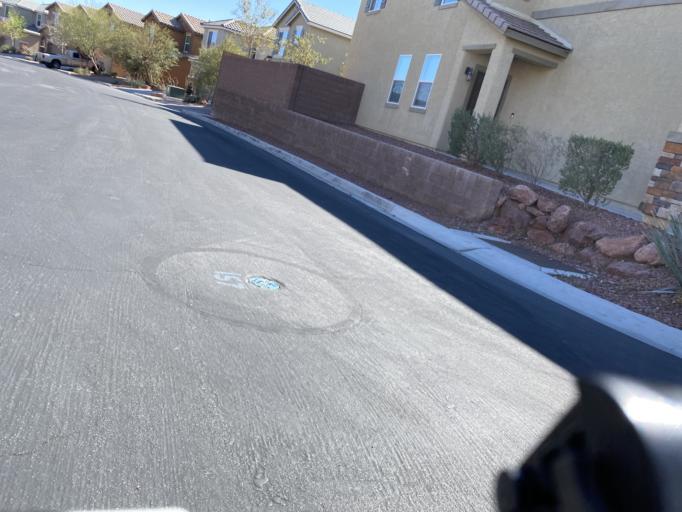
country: US
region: Nevada
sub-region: Clark County
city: Summerlin South
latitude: 36.3013
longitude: -115.3329
